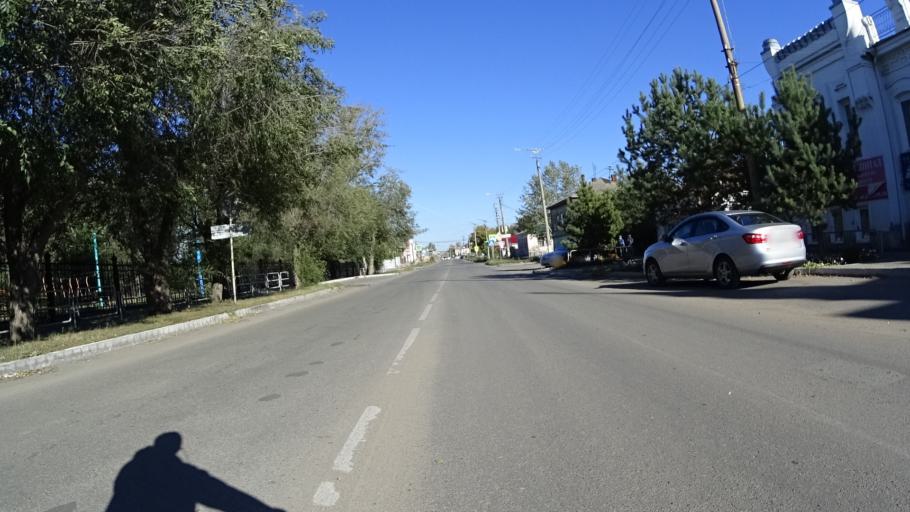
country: RU
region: Chelyabinsk
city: Troitsk
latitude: 54.0839
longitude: 61.5532
